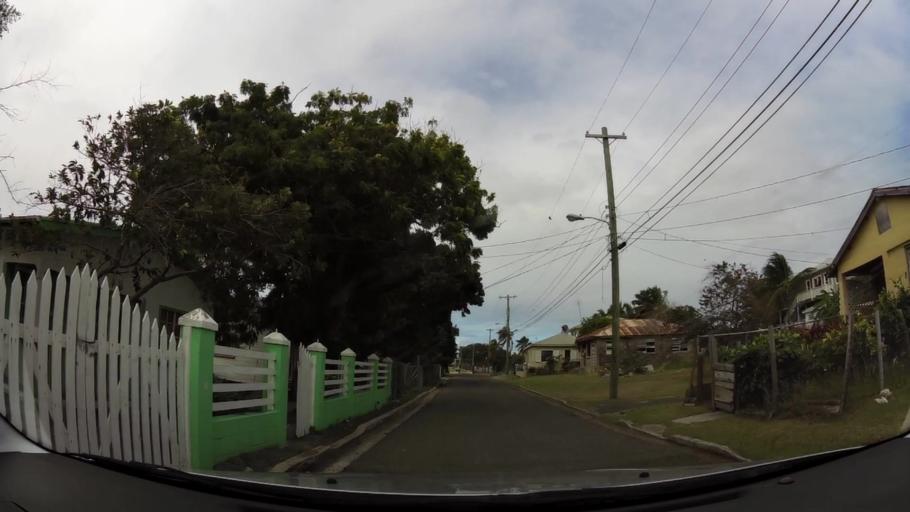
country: AG
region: Saint Peter
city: Parham
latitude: 17.0852
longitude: -61.7093
